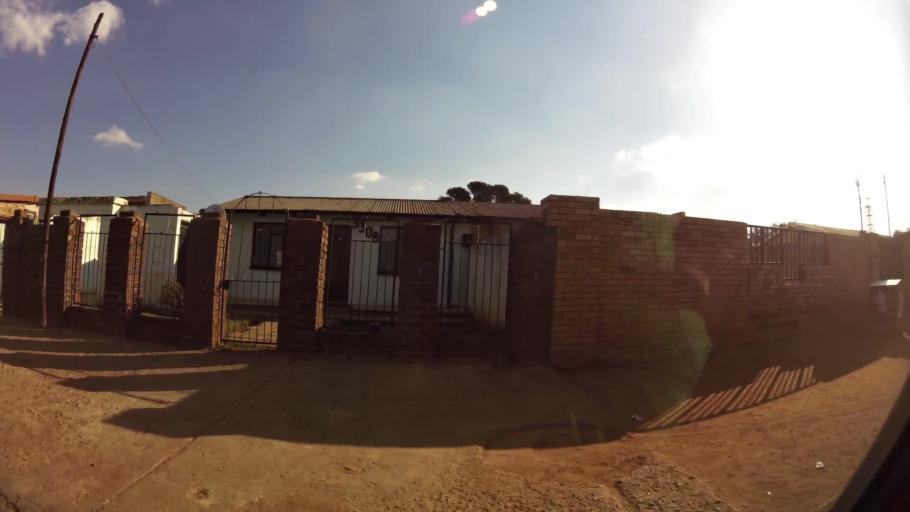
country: ZA
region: Gauteng
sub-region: City of Johannesburg Metropolitan Municipality
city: Soweto
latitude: -26.2188
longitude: 27.8722
